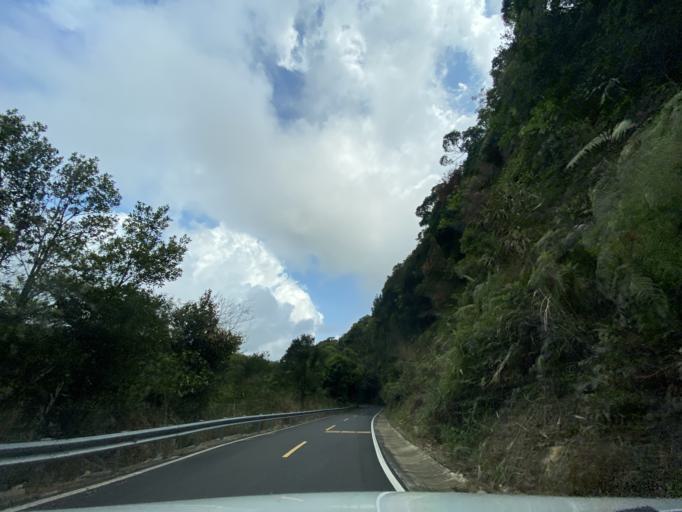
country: CN
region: Hainan
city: Diaoluoshan
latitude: 18.7192
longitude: 109.8771
